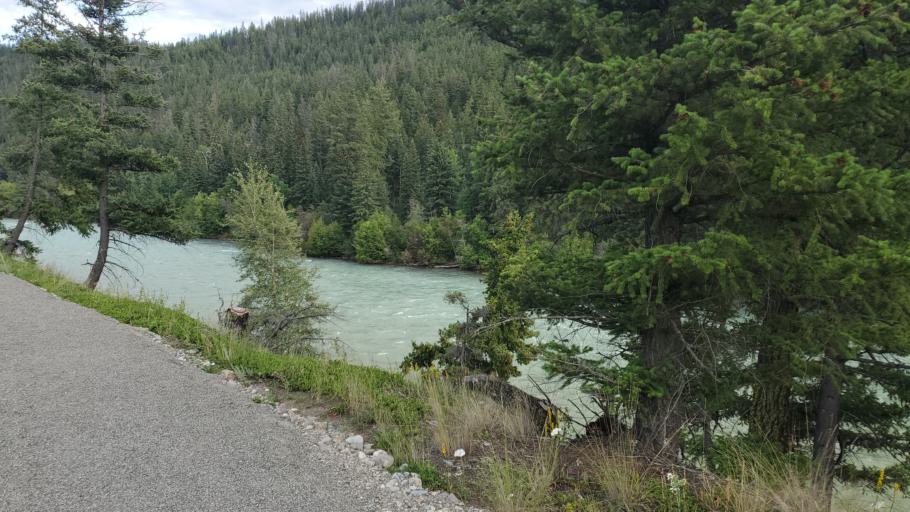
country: CA
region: British Columbia
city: Hanceville
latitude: 52.0863
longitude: -123.3924
